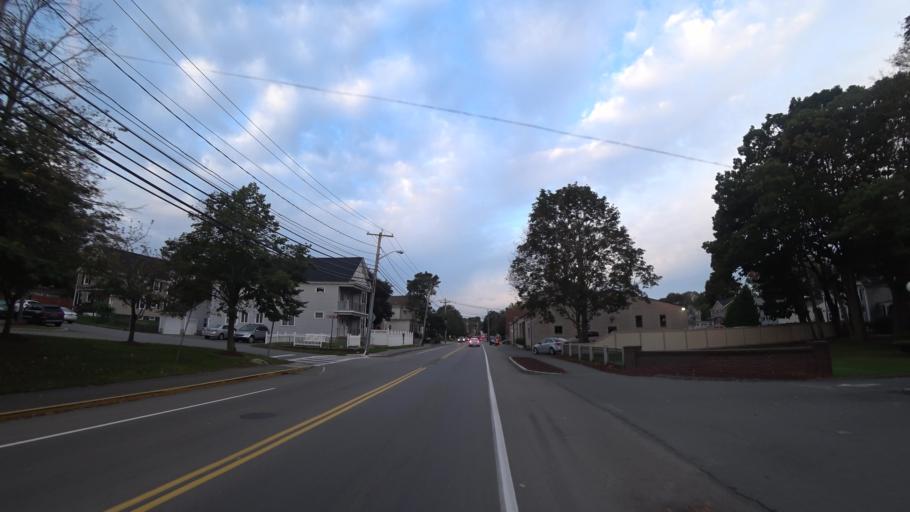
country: US
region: Massachusetts
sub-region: Essex County
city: Saugus
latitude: 42.4653
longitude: -71.0071
